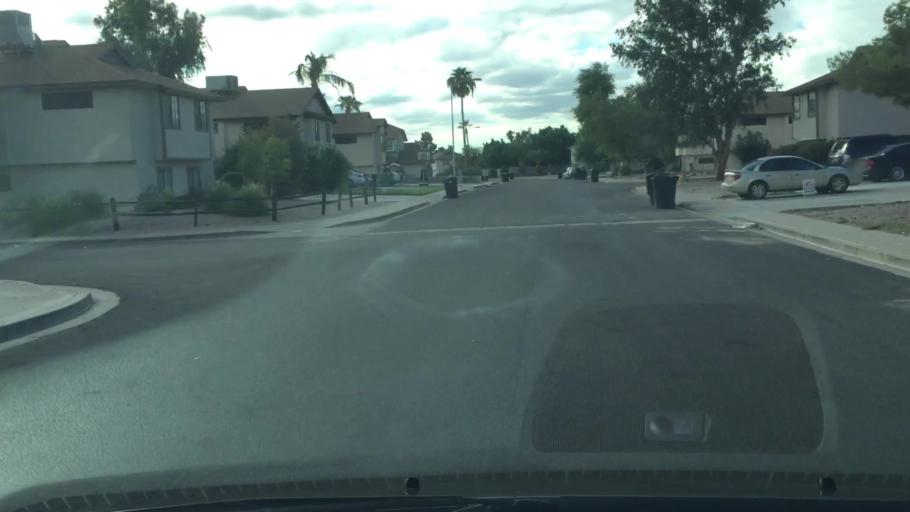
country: US
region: Arizona
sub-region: Maricopa County
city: Mesa
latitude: 33.4294
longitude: -111.7217
